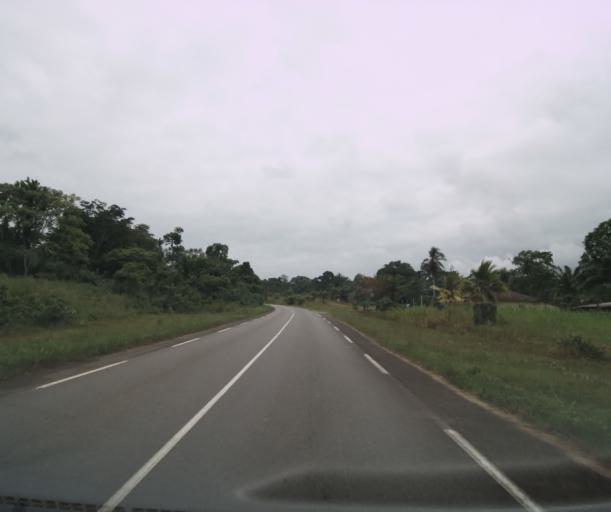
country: CM
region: South Province
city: Kribi
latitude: 3.1377
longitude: 10.0090
